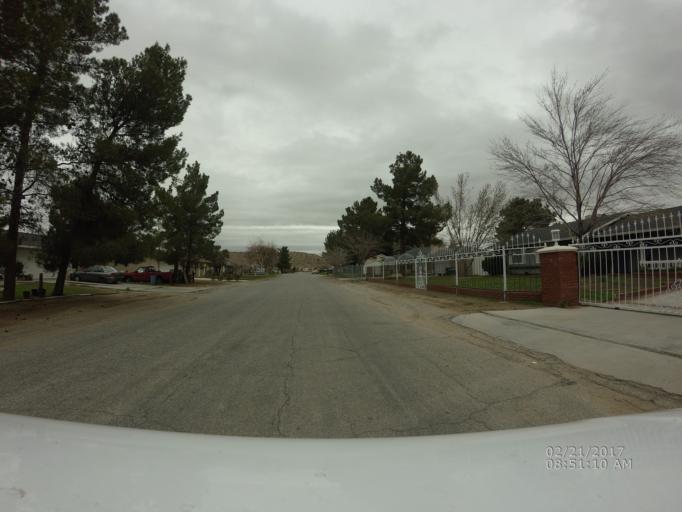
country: US
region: California
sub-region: Los Angeles County
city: Lake Los Angeles
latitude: 34.5961
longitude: -117.8279
